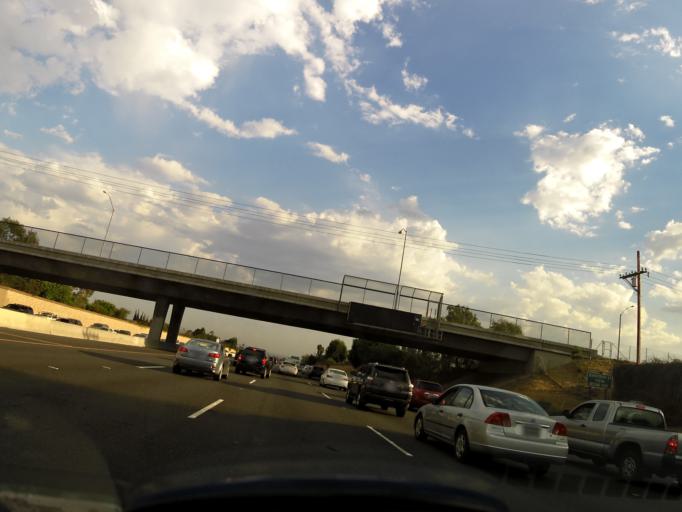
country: US
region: California
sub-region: Orange County
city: Tustin
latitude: 33.7676
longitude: -117.8311
